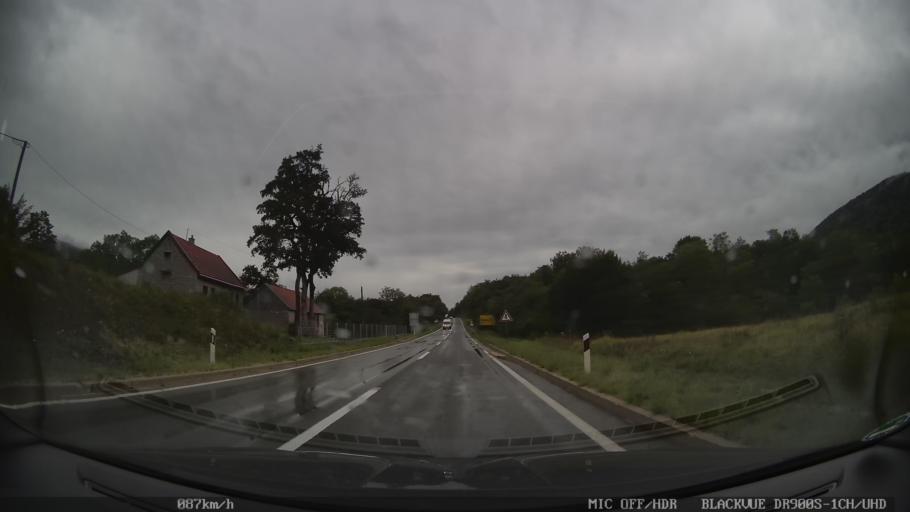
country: HR
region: Licko-Senjska
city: Brinje
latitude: 44.9641
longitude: 15.0794
